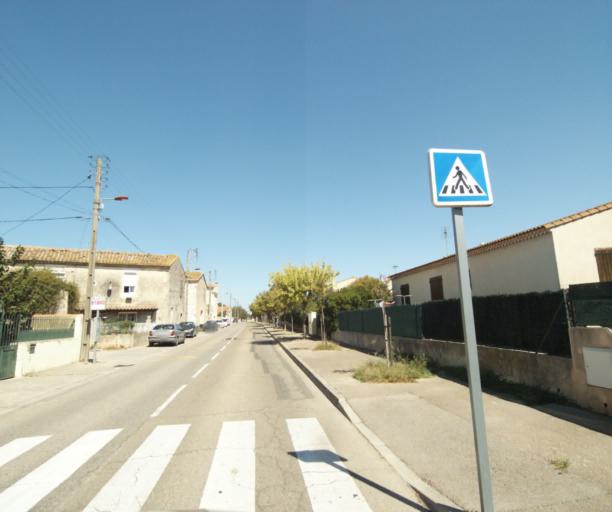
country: FR
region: Languedoc-Roussillon
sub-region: Departement du Gard
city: Rodilhan
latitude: 43.8283
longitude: 4.4305
